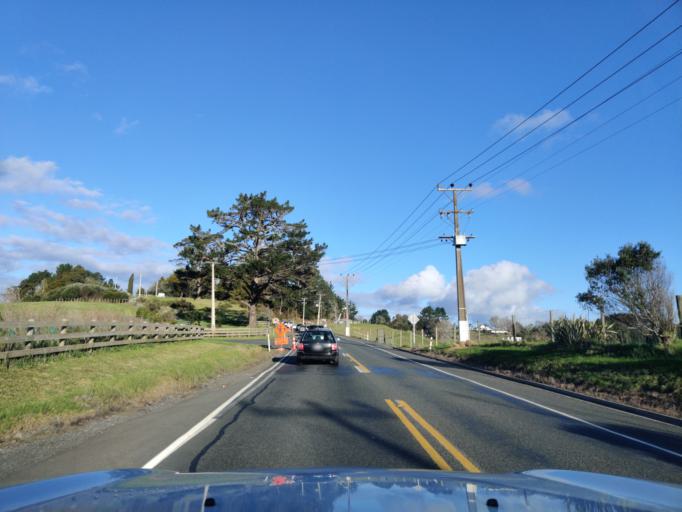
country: NZ
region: Auckland
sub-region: Auckland
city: Red Hill
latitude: -36.9670
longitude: 174.9837
